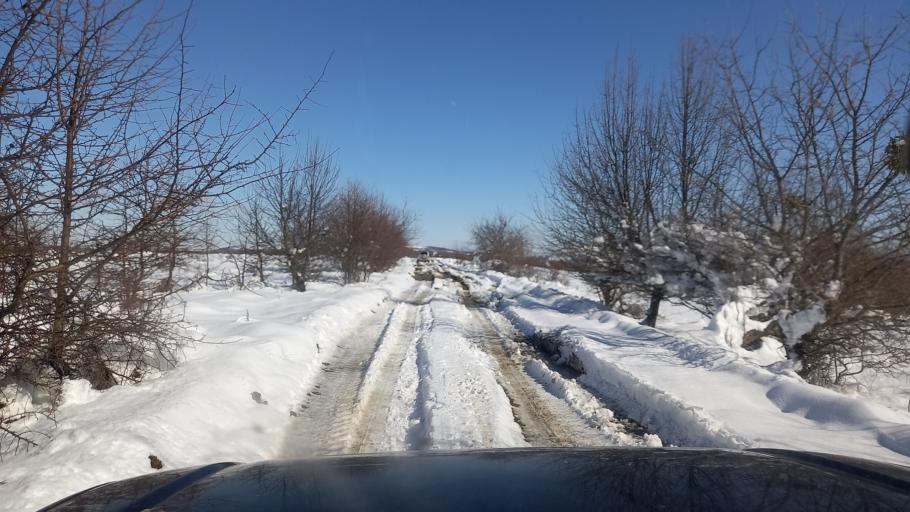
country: RU
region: Krasnodarskiy
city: Gubskaya
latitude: 44.3380
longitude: 40.4319
